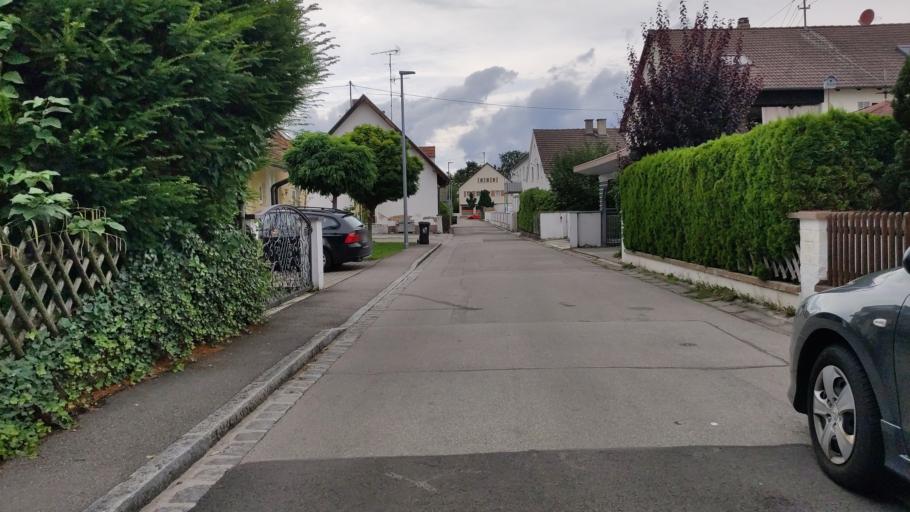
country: DE
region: Bavaria
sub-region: Swabia
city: Konigsbrunn
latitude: 48.2734
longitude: 10.8914
